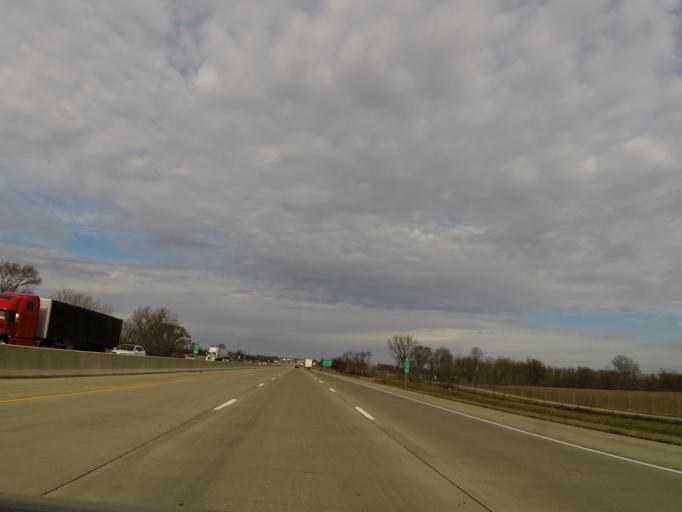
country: US
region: Illinois
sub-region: Winnebago County
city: South Beloit
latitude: 42.4737
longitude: -88.9950
